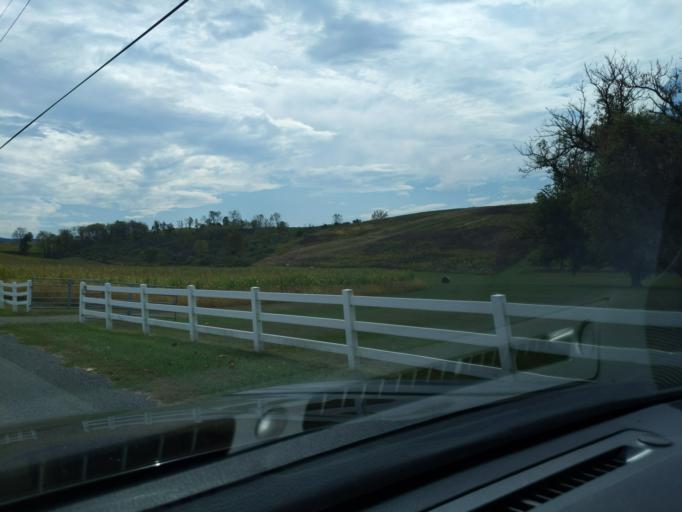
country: US
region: Pennsylvania
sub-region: Blair County
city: Hollidaysburg
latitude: 40.4227
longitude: -78.3445
